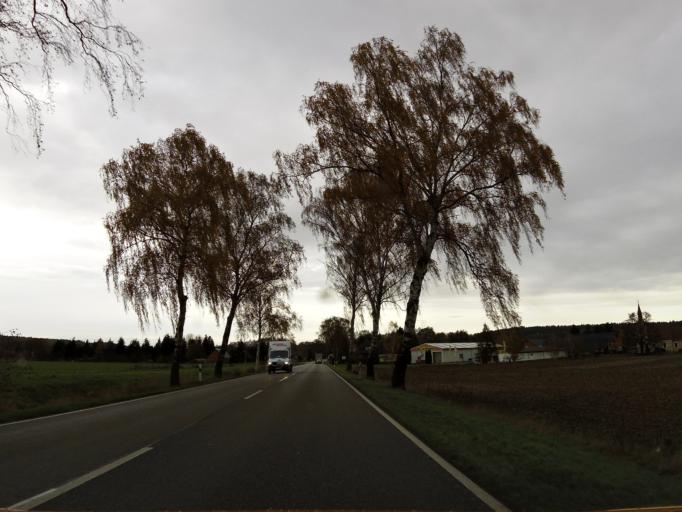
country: DE
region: Saxony-Anhalt
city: Kalbe
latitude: 52.5971
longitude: 11.3340
